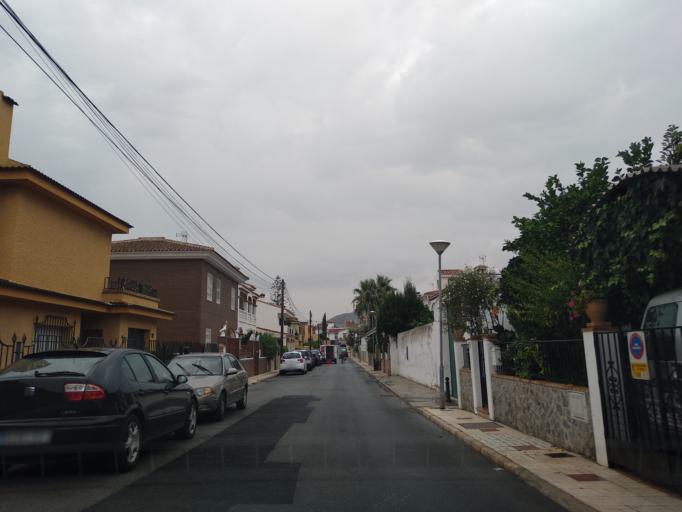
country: ES
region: Andalusia
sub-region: Provincia de Malaga
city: Malaga
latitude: 36.7374
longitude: -4.4776
